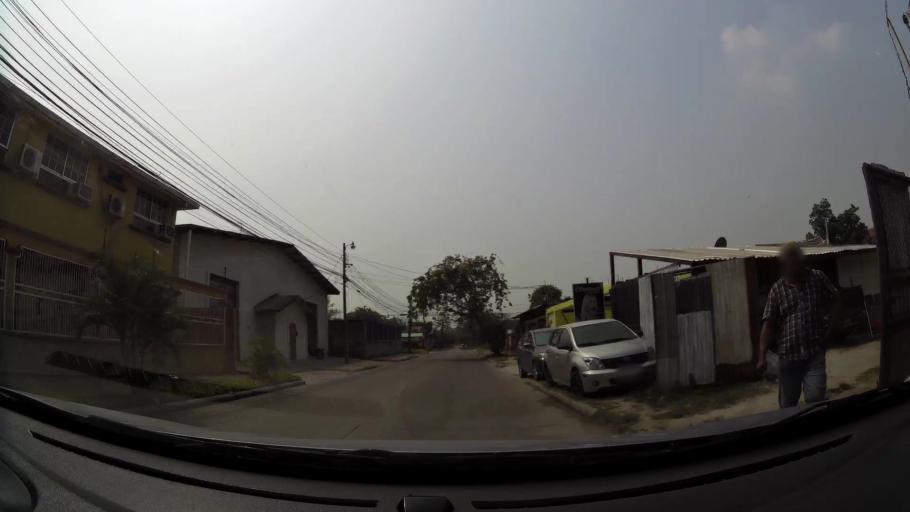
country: HN
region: Cortes
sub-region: San Pedro Sula
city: Pena Blanca
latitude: 15.5495
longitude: -88.0266
